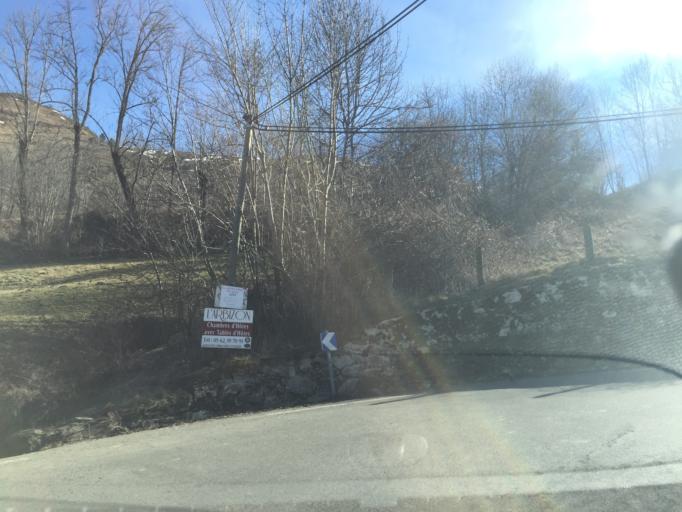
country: FR
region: Midi-Pyrenees
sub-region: Departement des Hautes-Pyrenees
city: Saint-Lary-Soulan
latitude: 42.8130
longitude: 0.3503
